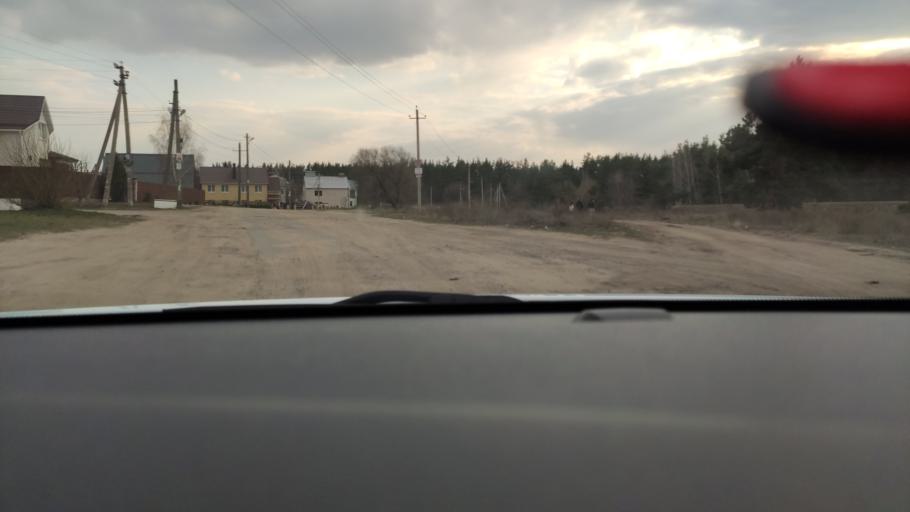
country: RU
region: Voronezj
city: Pridonskoy
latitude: 51.6350
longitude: 39.0870
